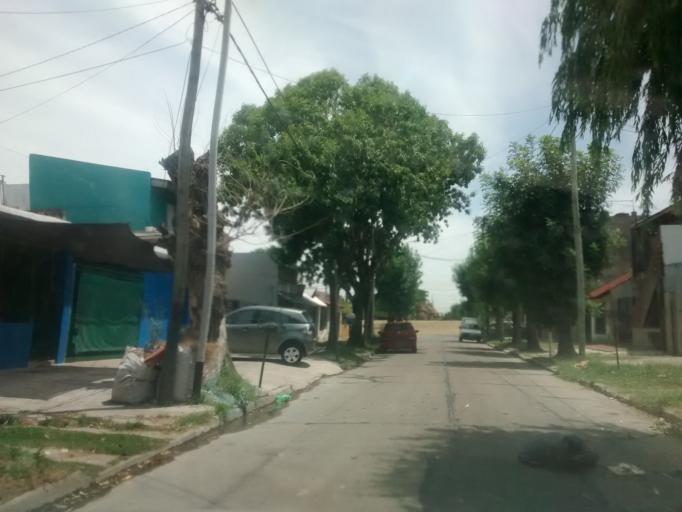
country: AR
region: Buenos Aires
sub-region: Partido de Avellaneda
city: Avellaneda
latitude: -34.6892
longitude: -58.3235
